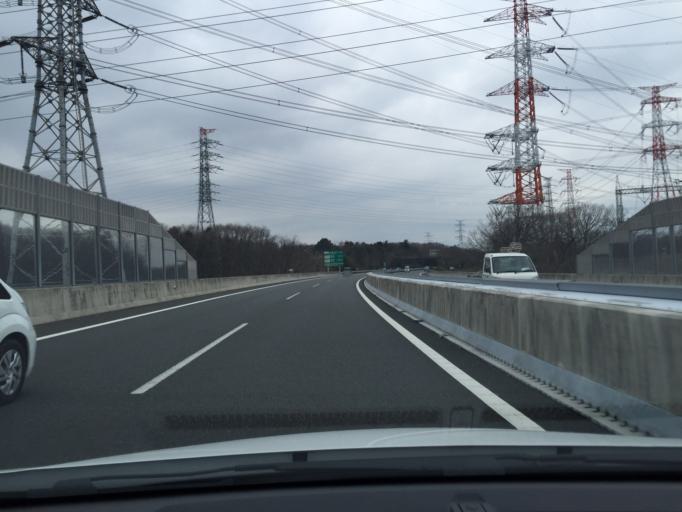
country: JP
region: Saitama
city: Sakado
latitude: 35.9625
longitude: 139.4391
